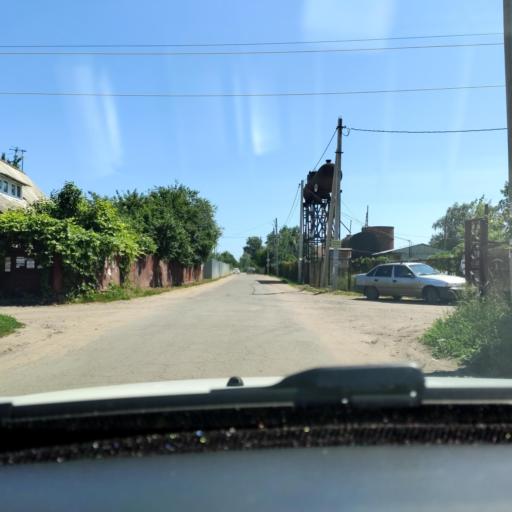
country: RU
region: Voronezj
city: Shilovo
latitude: 51.5875
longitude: 39.1553
